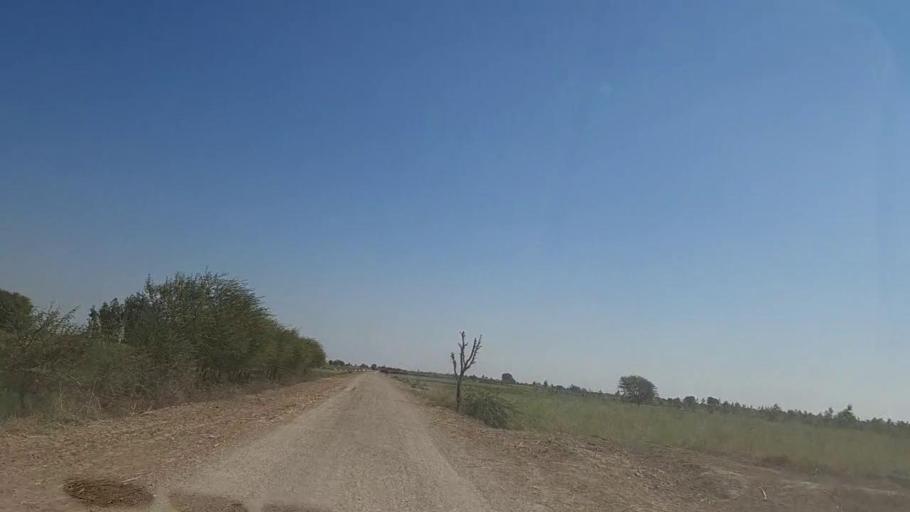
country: PK
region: Sindh
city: Digri
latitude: 25.1105
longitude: 69.1184
